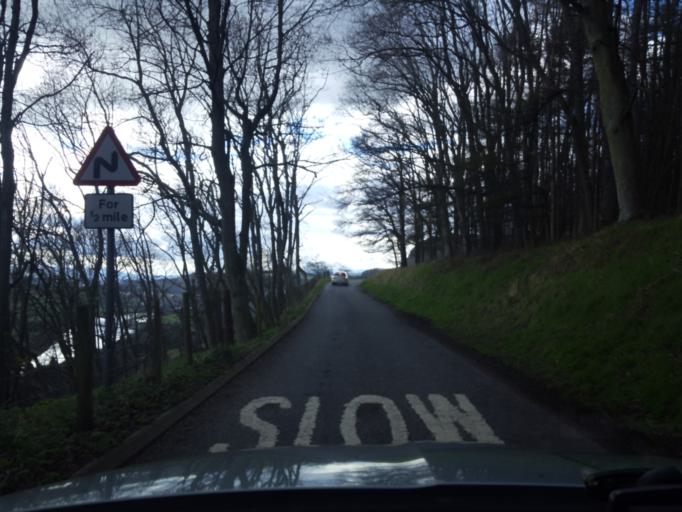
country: GB
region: Scotland
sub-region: Perth and Kinross
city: Scone
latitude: 56.3907
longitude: -3.3704
